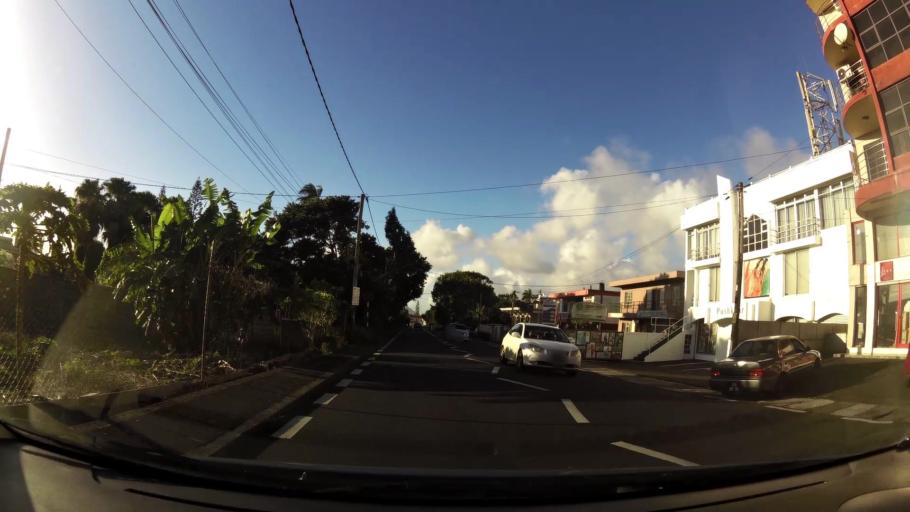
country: MU
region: Plaines Wilhems
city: Curepipe
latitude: -20.3088
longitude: 57.5249
